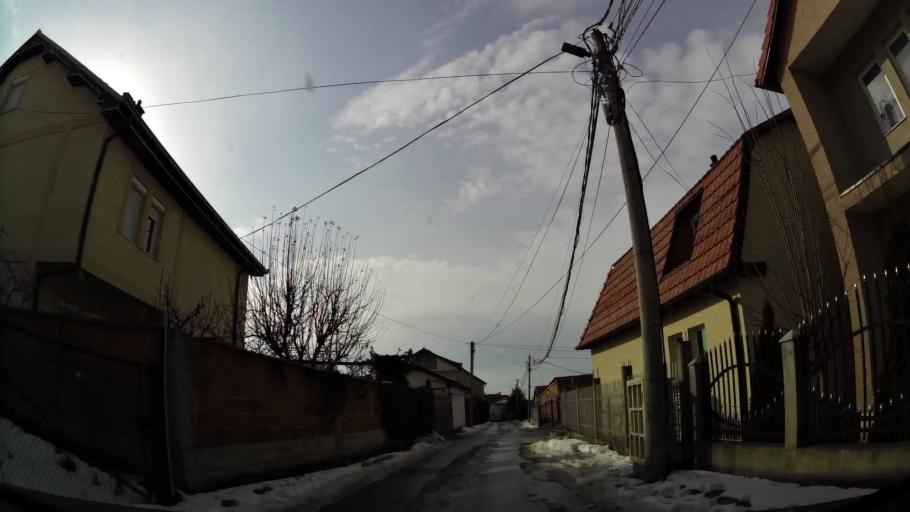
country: XK
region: Pristina
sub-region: Komuna e Prishtines
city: Pristina
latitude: 42.6904
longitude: 21.1568
